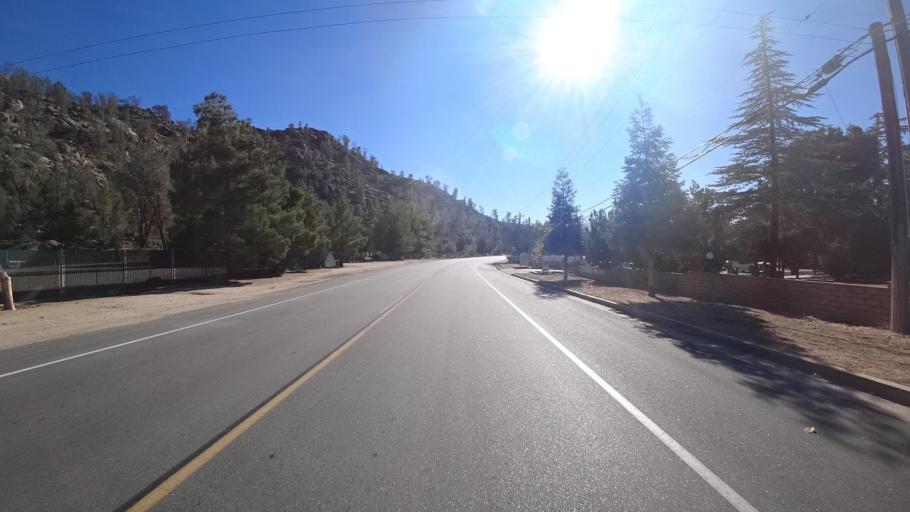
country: US
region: California
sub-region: Kern County
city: Kernville
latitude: 35.7360
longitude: -118.4142
